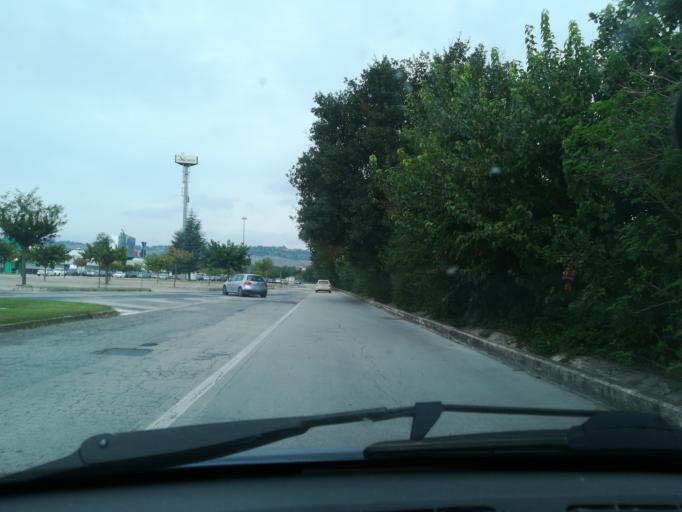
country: IT
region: The Marches
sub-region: Provincia di Macerata
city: Piediripa
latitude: 43.2792
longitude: 13.5051
